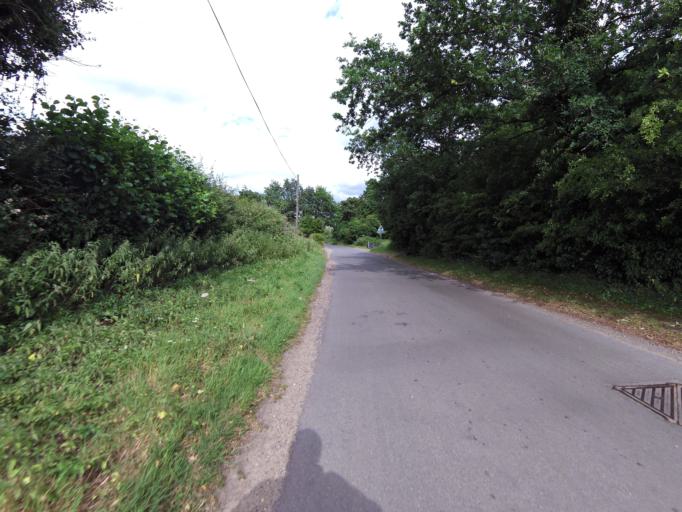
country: GB
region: England
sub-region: Suffolk
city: Beccles
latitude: 52.4695
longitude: 1.5105
